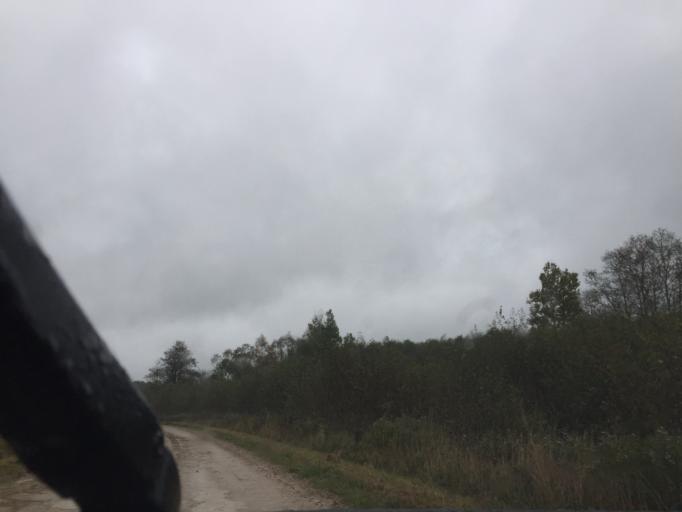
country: LV
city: Tireli
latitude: 56.7519
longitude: 23.5357
